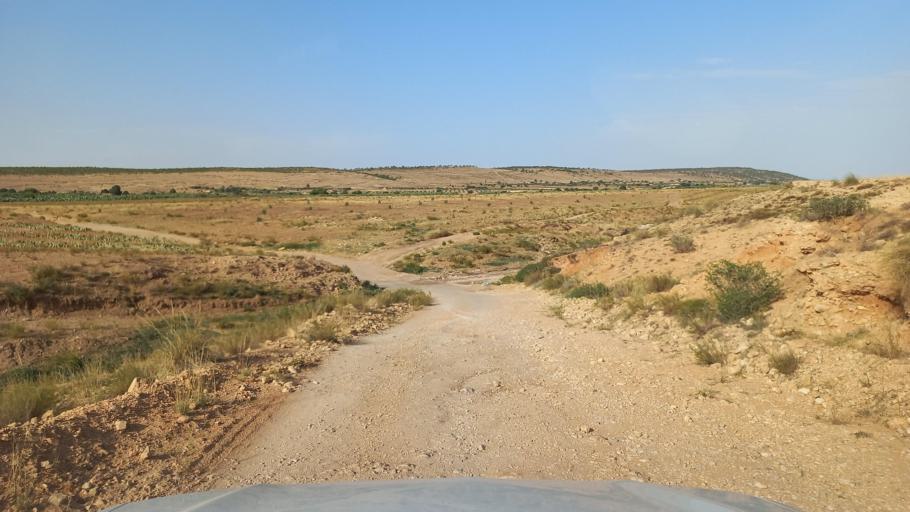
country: TN
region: Al Qasrayn
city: Kasserine
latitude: 35.3567
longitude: 8.8526
